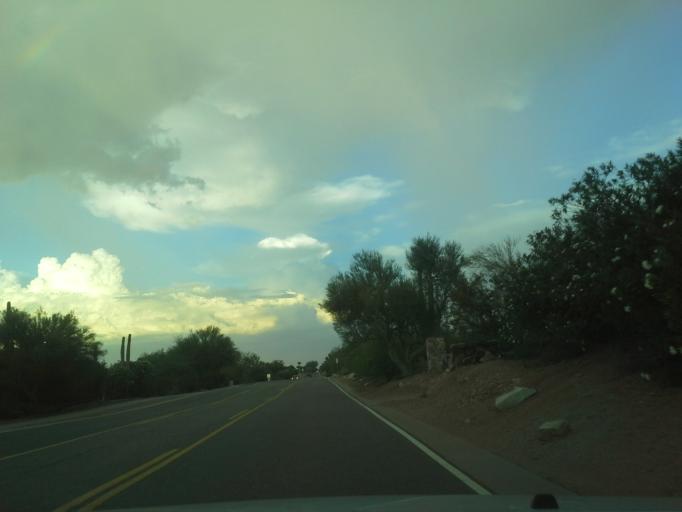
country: US
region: Arizona
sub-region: Maricopa County
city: Paradise Valley
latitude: 33.5237
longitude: -111.9678
